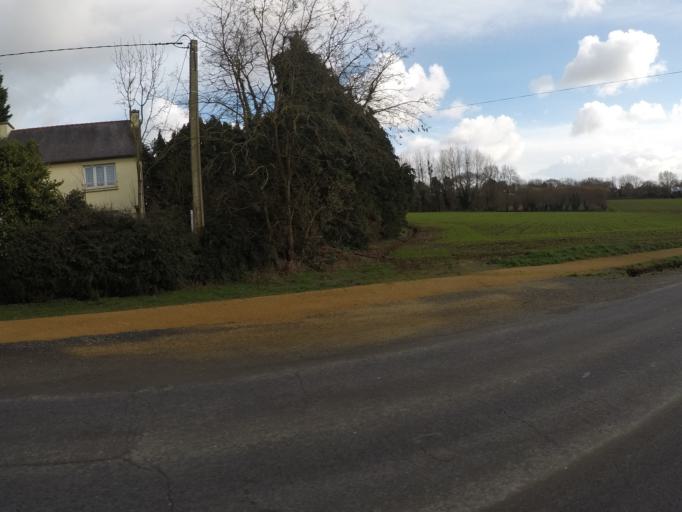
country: FR
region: Brittany
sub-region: Departement des Cotes-d'Armor
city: Lanvollon
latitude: 48.6197
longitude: -2.9856
